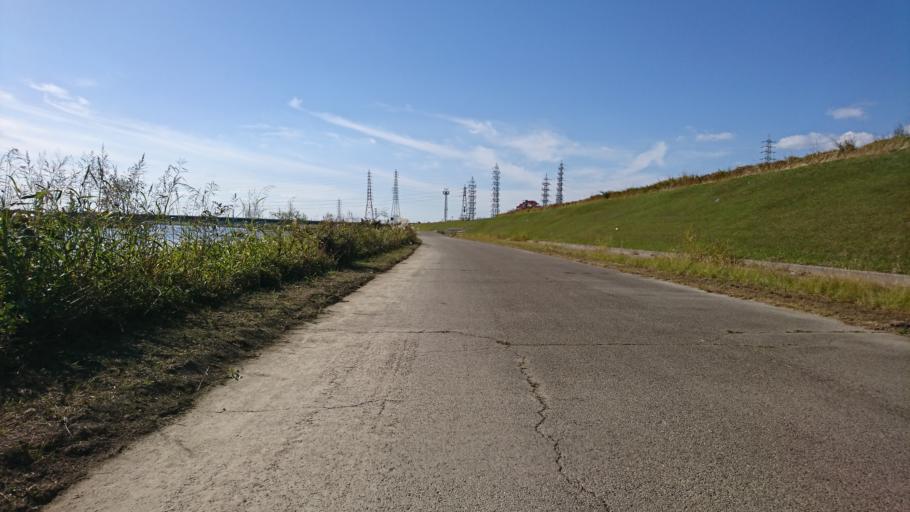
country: JP
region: Hyogo
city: Kakogawacho-honmachi
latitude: 34.7711
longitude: 134.8129
